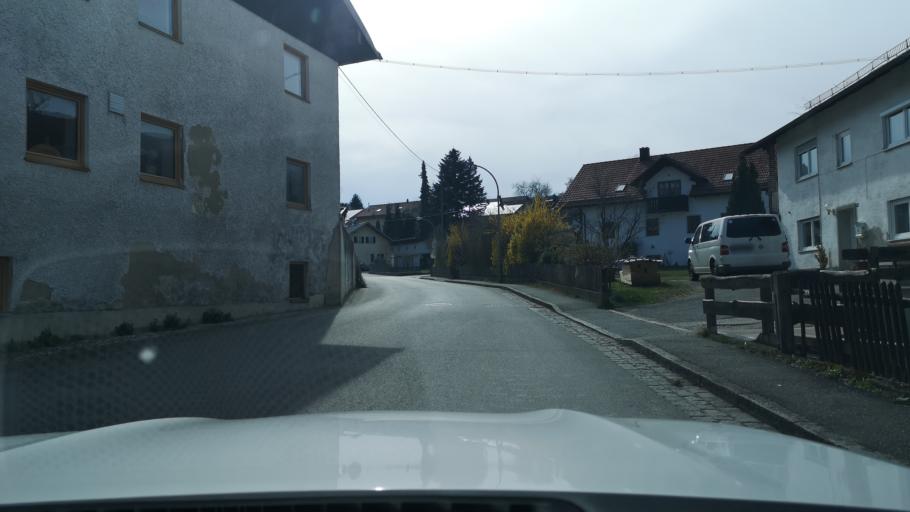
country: DE
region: Bavaria
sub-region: Upper Bavaria
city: Isen
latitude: 48.1891
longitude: 12.0490
